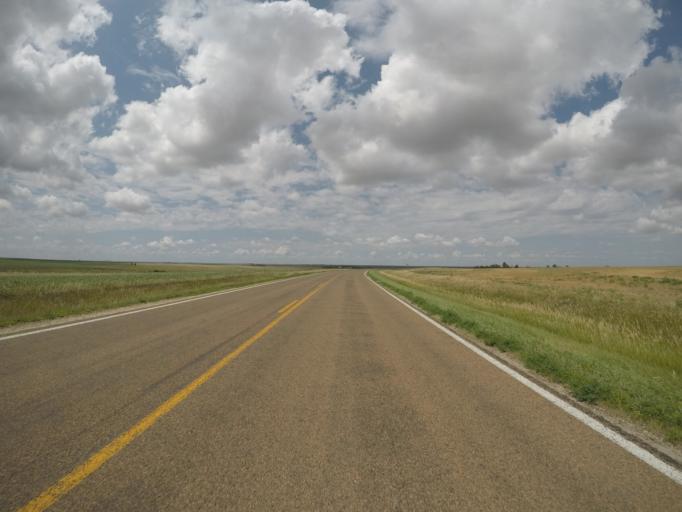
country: US
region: Kansas
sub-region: Rawlins County
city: Atwood
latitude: 39.9126
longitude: -101.0550
